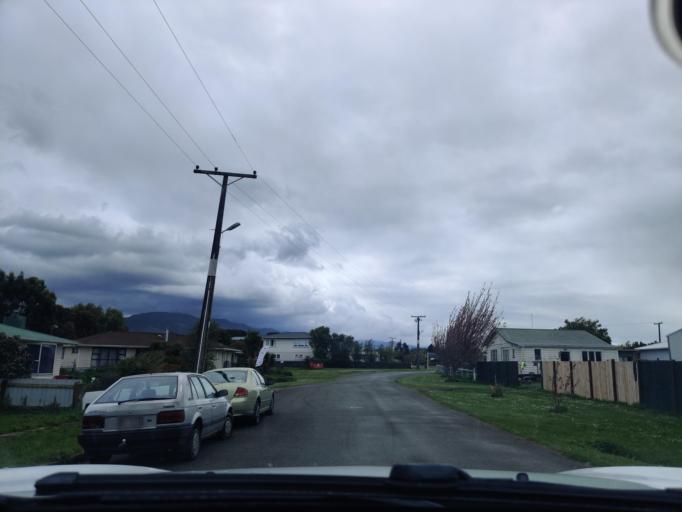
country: NZ
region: Manawatu-Wanganui
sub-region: Palmerston North City
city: Palmerston North
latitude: -40.3351
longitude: 175.8644
